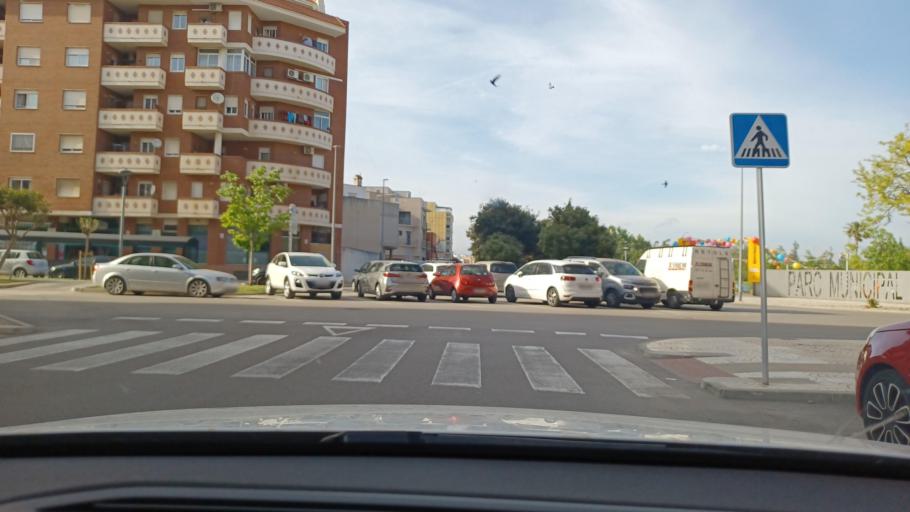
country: ES
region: Catalonia
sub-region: Provincia de Tarragona
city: Amposta
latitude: 40.7034
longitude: 0.5818
